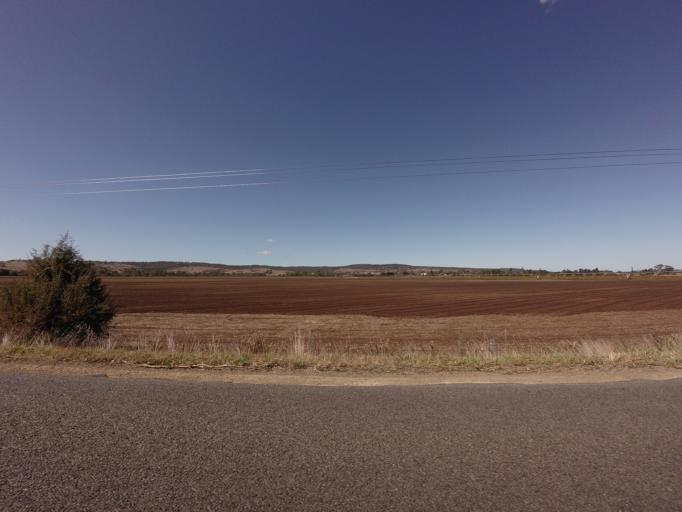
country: AU
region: Tasmania
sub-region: Break O'Day
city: St Helens
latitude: -41.9974
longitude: 148.0714
